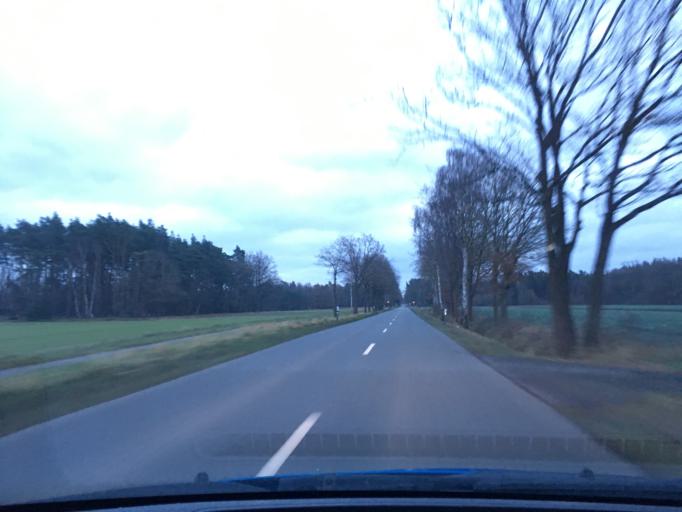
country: DE
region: Lower Saxony
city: Vogelsen
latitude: 53.2977
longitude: 10.3465
